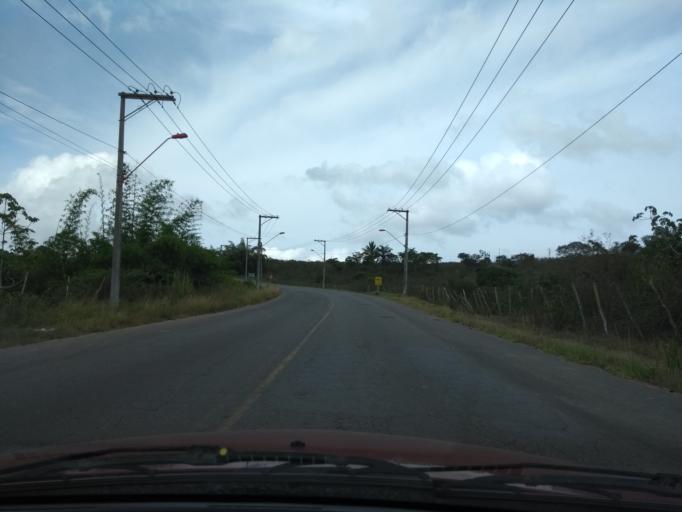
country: BR
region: Bahia
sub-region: Sao Francisco Do Conde
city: Sao Francisco do Conde
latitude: -12.6107
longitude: -38.6521
